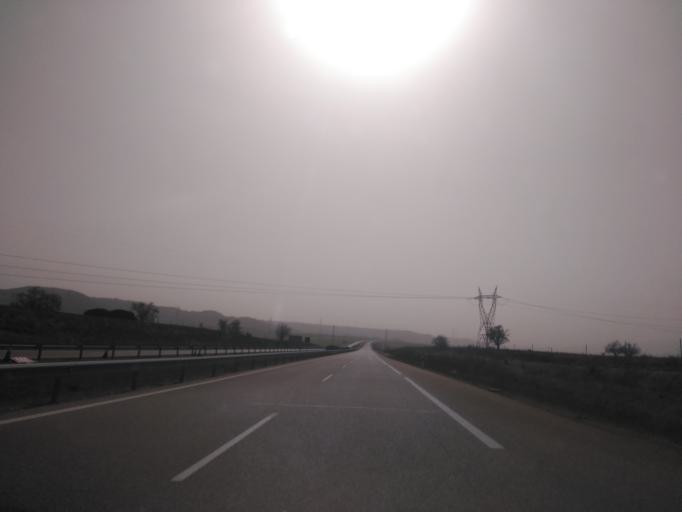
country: ES
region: Castille and Leon
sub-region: Provincia de Palencia
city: Fuentes de Valdepero
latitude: 42.0539
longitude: -4.4921
